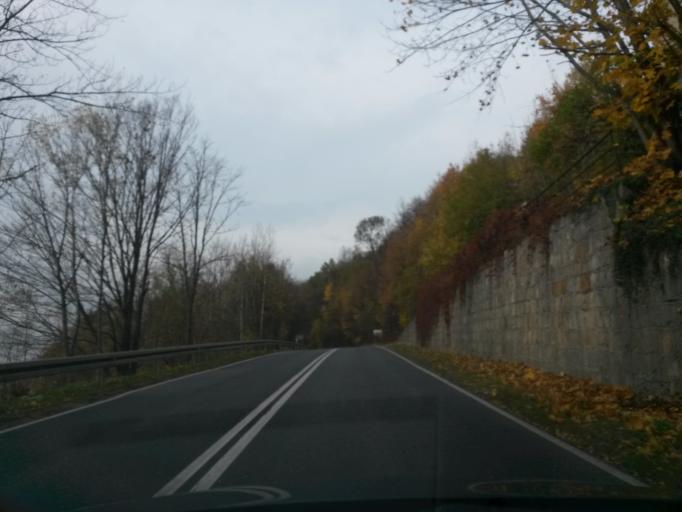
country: PL
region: Lower Silesian Voivodeship
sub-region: Powiat klodzki
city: Klodzko
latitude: 50.3807
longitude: 16.6695
